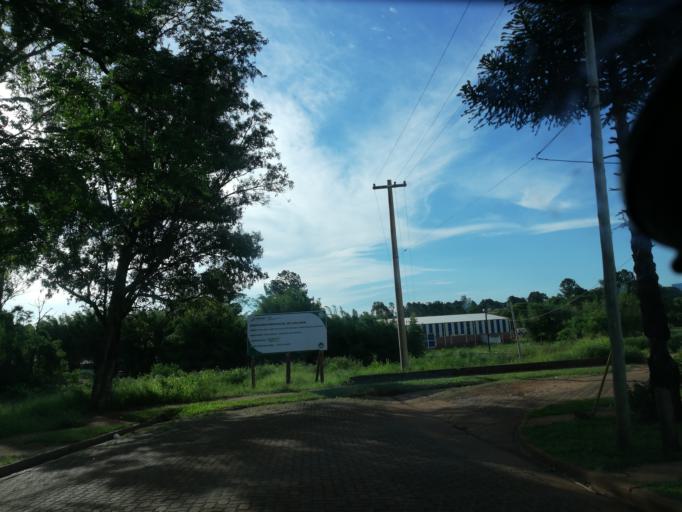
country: AR
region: Misiones
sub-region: Departamento de Capital
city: Posadas
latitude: -27.4056
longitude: -55.9579
